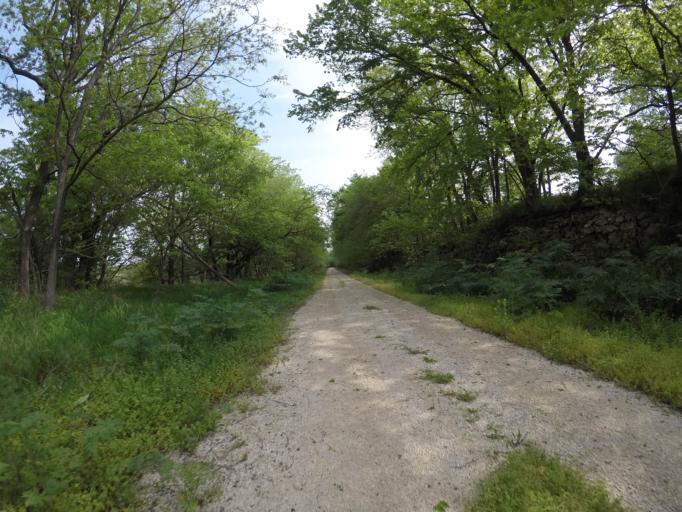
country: US
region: Nebraska
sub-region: Gage County
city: Wymore
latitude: 40.0157
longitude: -96.5924
